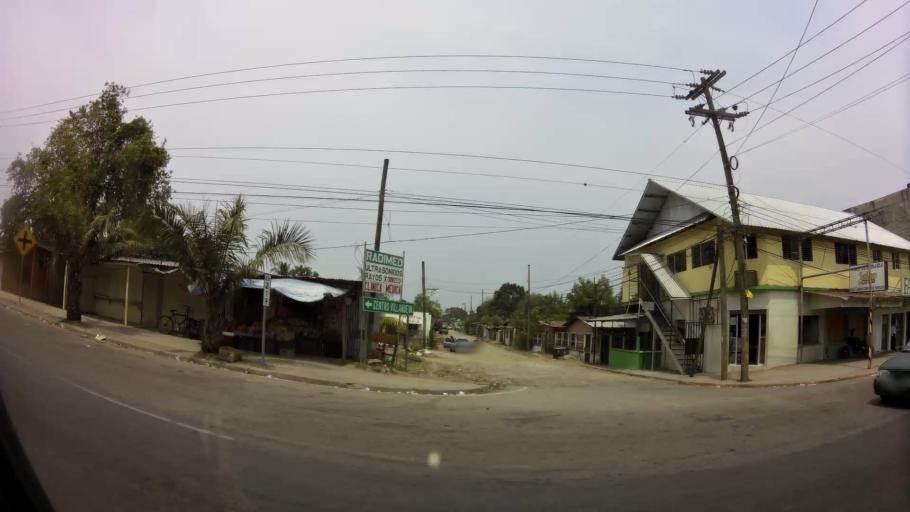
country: HN
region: Cortes
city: Villanueva
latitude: 15.3172
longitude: -87.9906
